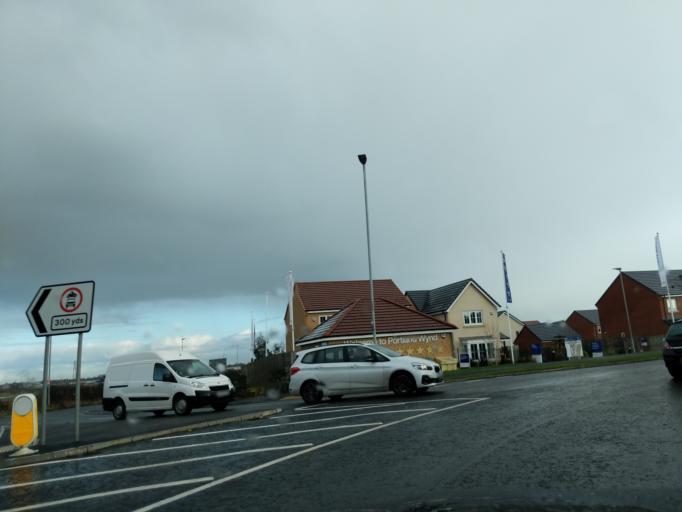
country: GB
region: England
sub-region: Northumberland
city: Seaton Delaval
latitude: 55.1044
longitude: -1.5416
